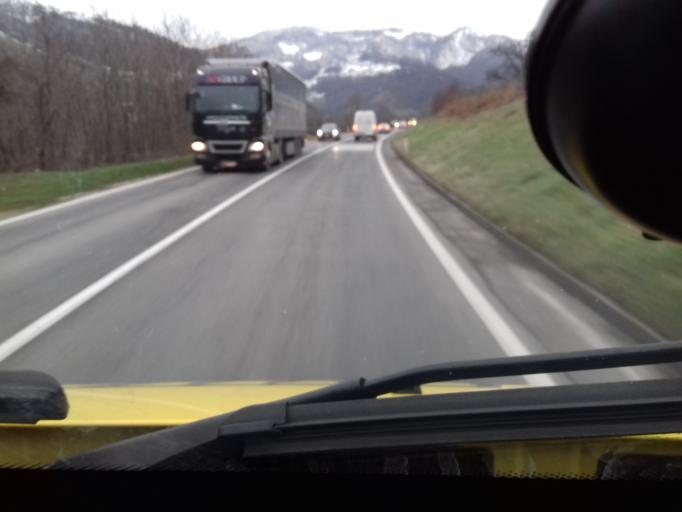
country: BA
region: Federation of Bosnia and Herzegovina
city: Zepce
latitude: 44.3690
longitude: 18.0032
